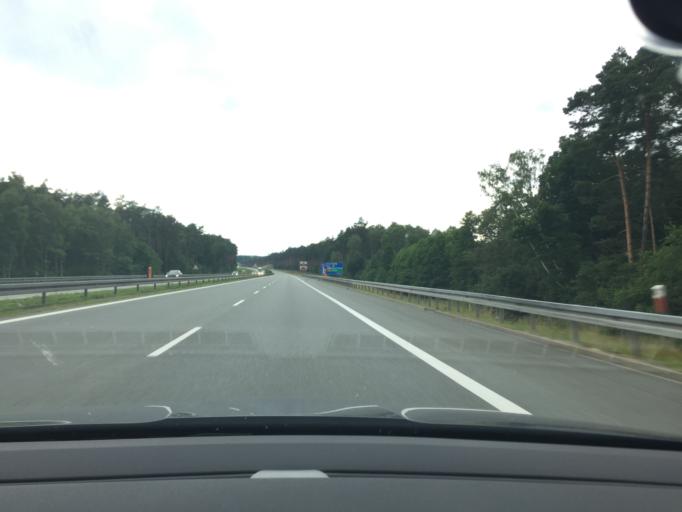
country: PL
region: Greater Poland Voivodeship
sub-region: Powiat nowotomyski
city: Nowy Tomysl
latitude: 52.3643
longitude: 16.1334
